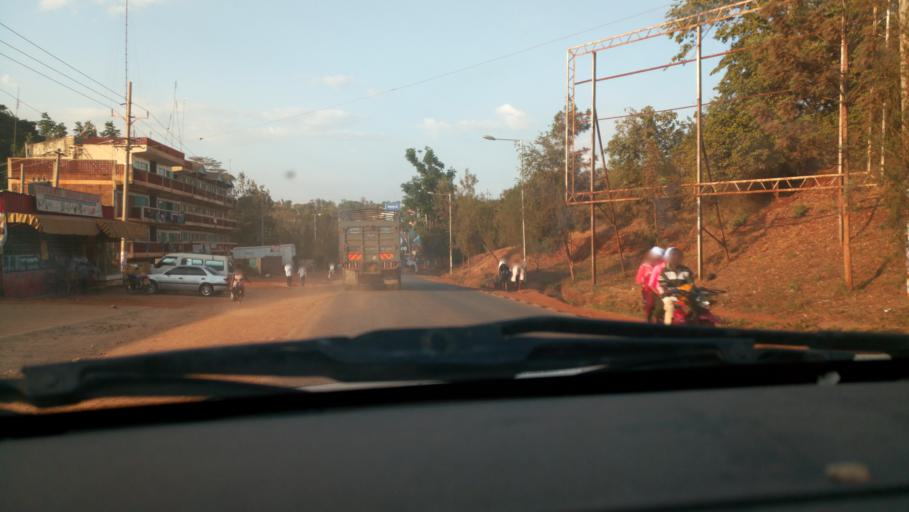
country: KE
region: Murang'a District
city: Murang'a
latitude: -0.7271
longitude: 37.1525
